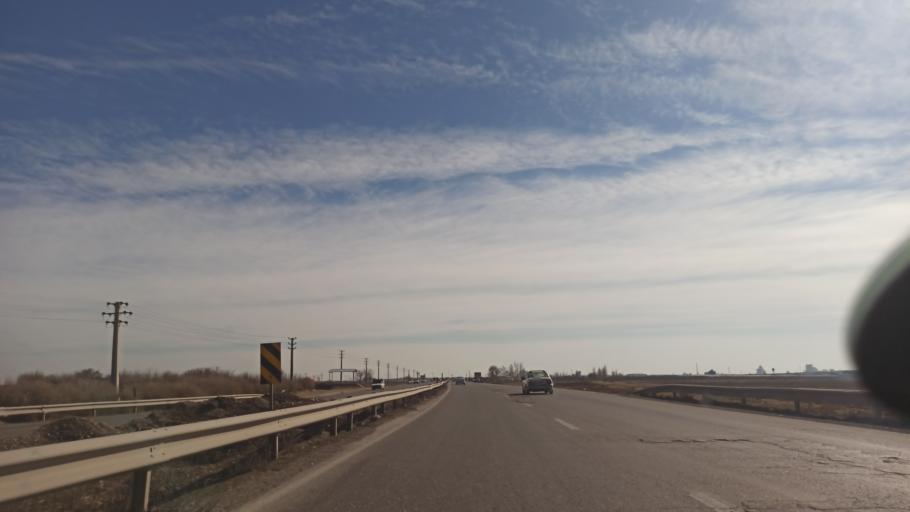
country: IR
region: Qazvin
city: Alvand
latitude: 36.1505
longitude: 50.0219
